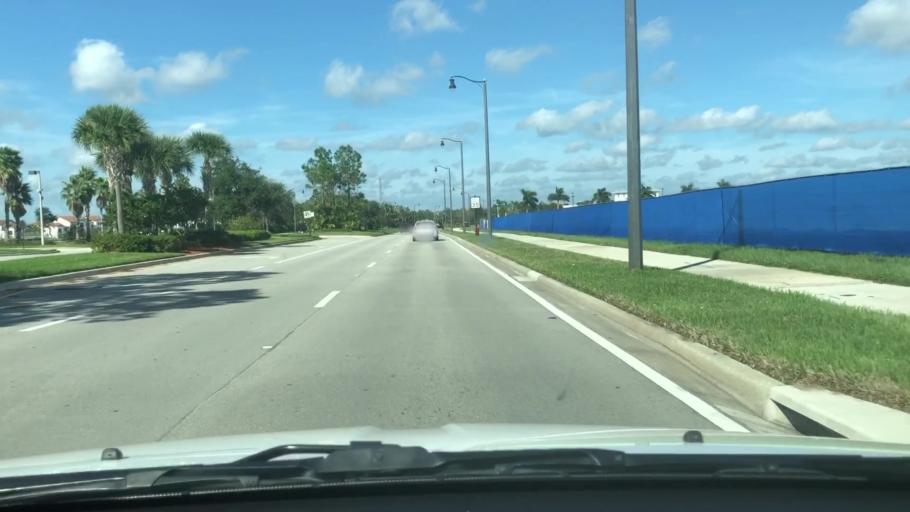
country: US
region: Florida
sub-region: Saint Lucie County
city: Port Saint Lucie
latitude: 27.2738
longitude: -80.4304
